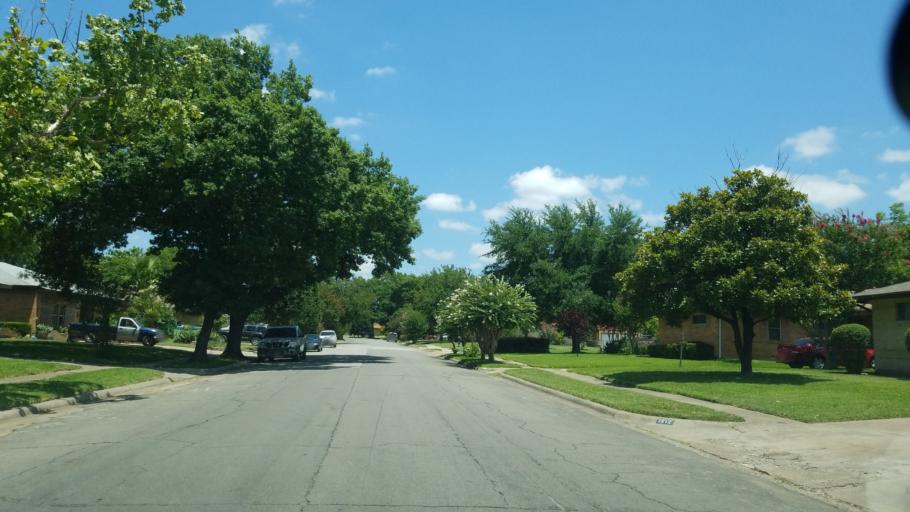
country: US
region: Texas
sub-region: Dallas County
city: Balch Springs
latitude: 32.7380
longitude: -96.7057
